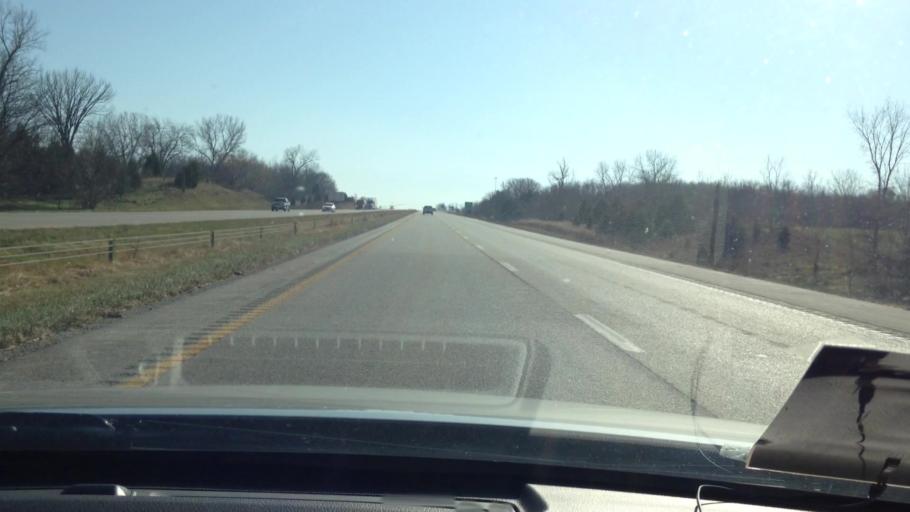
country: US
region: Missouri
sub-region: Platte County
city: Platte City
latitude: 39.4381
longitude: -94.7894
